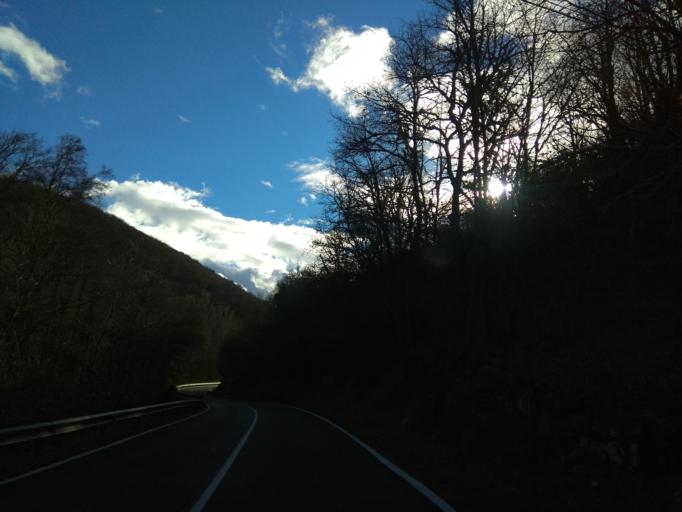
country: ES
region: Cantabria
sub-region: Provincia de Cantabria
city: San Martin de Elines
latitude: 42.8687
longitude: -3.9126
